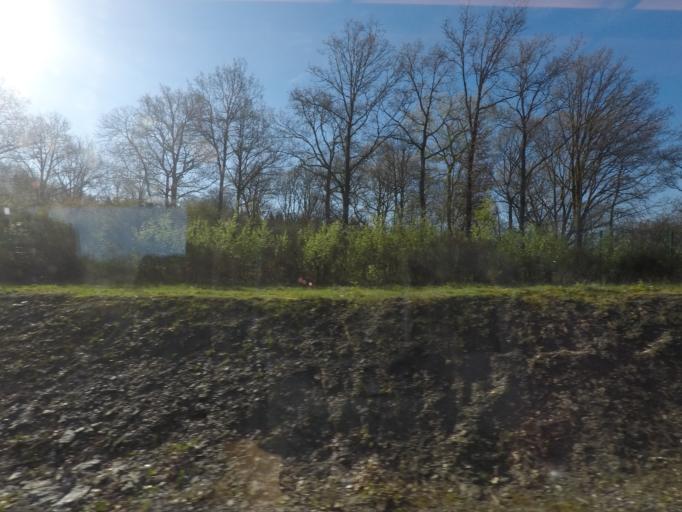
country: BE
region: Wallonia
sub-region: Province de Namur
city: Rochefort
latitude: 50.2455
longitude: 5.2242
